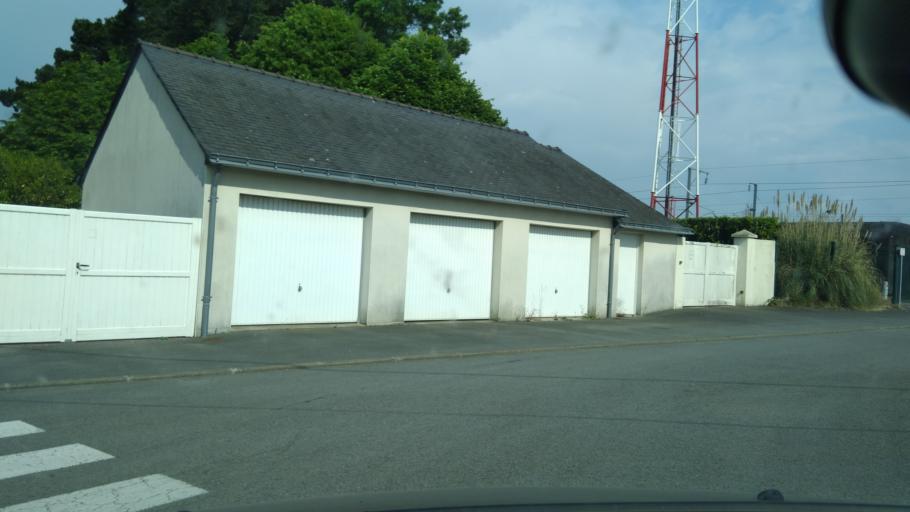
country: FR
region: Pays de la Loire
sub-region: Departement de la Loire-Atlantique
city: Montoir-de-Bretagne
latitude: 47.3215
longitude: -2.1619
